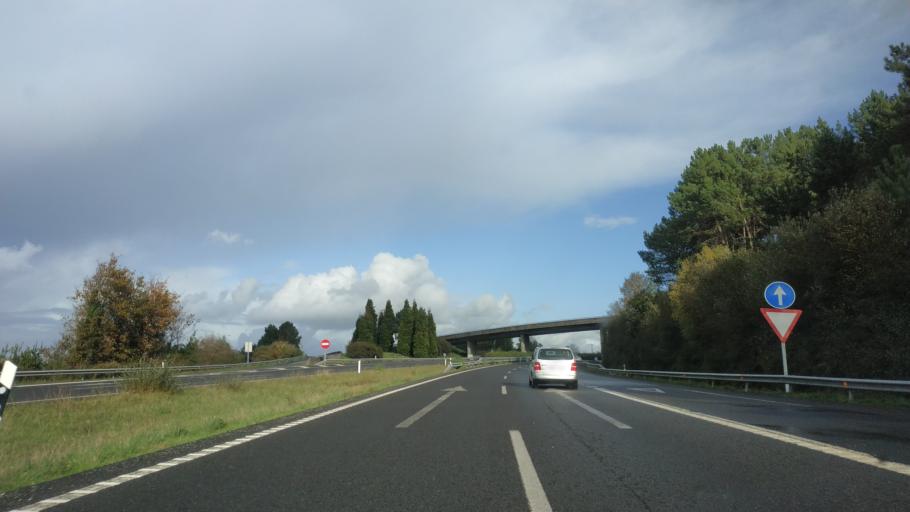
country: ES
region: Galicia
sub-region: Provincia da Coruna
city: Culleredo
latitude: 43.2733
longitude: -8.3712
